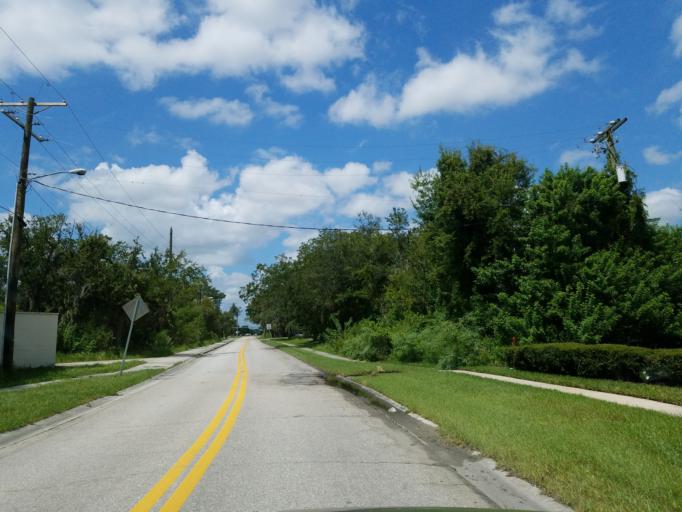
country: US
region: Florida
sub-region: Hillsborough County
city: Mango
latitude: 27.9412
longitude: -82.3327
